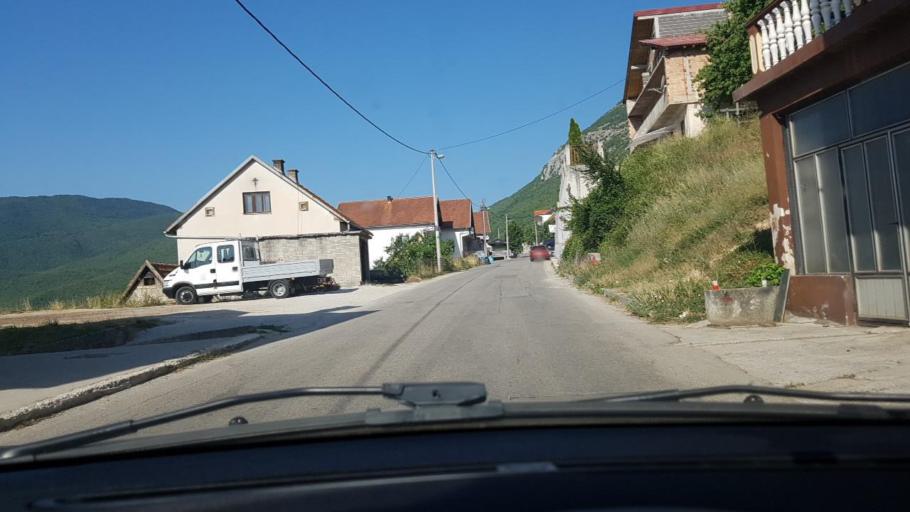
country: BA
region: Federation of Bosnia and Herzegovina
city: Rumboci
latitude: 43.8292
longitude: 17.5001
